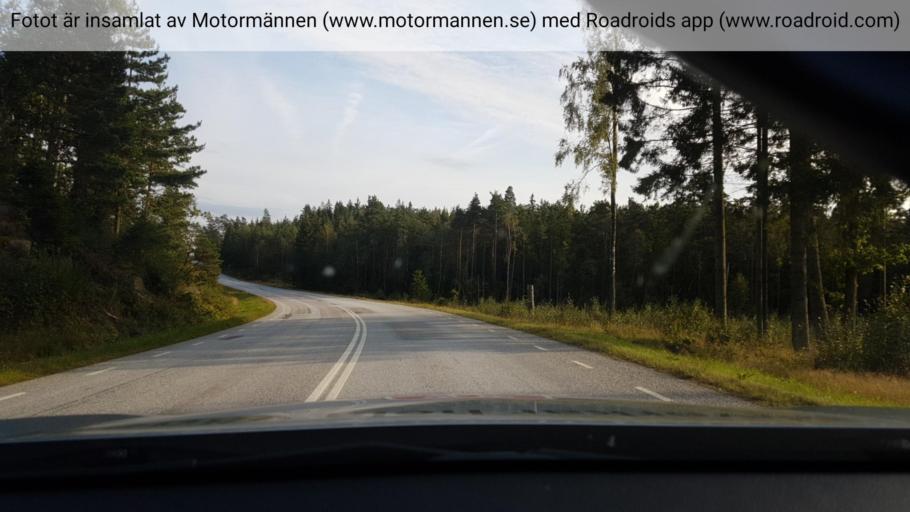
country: SE
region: Vaestra Goetaland
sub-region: Uddevalla Kommun
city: Ljungskile
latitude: 58.1379
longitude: 11.9756
